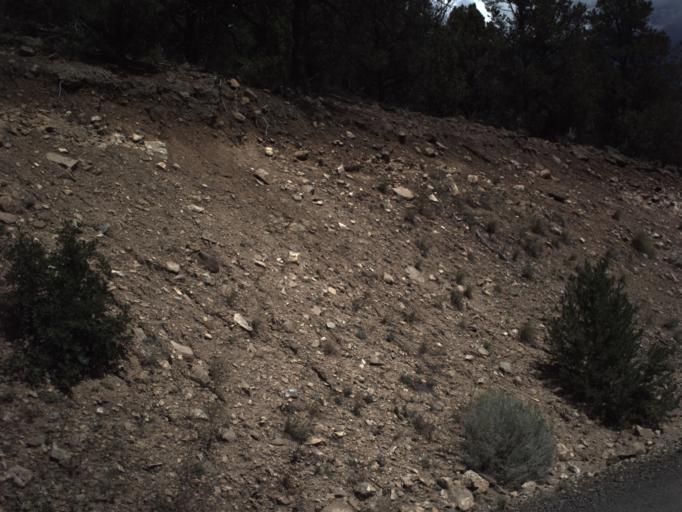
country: US
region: Utah
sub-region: Piute County
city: Junction
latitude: 38.2574
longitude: -112.3077
